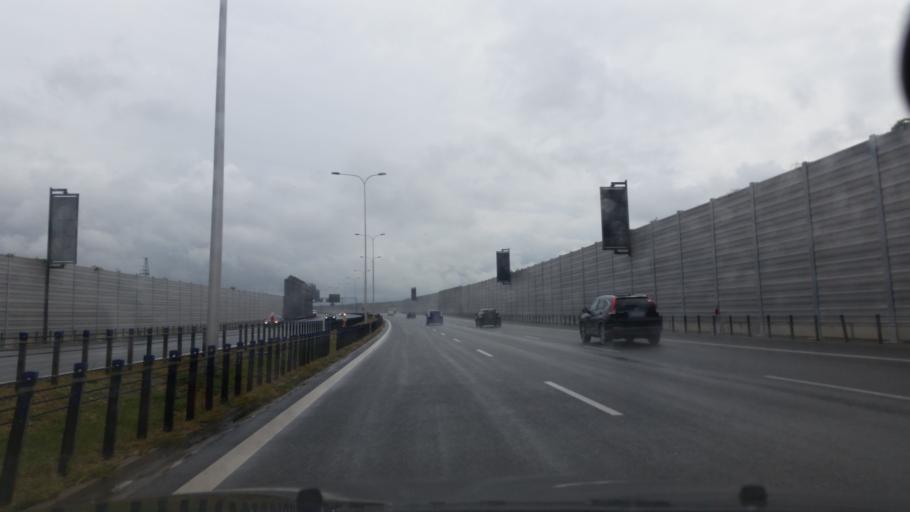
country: PL
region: Masovian Voivodeship
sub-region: Powiat pruszkowski
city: Piastow
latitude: 52.1937
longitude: 20.8558
